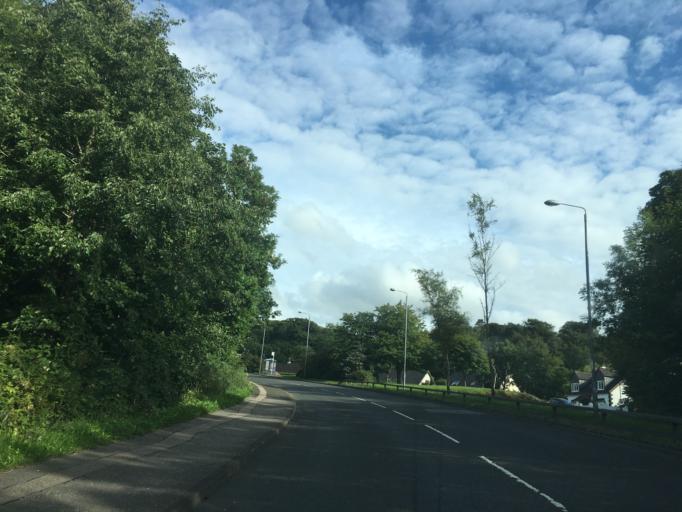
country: GB
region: Scotland
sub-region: Argyll and Bute
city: Oban
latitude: 56.4007
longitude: -5.4726
